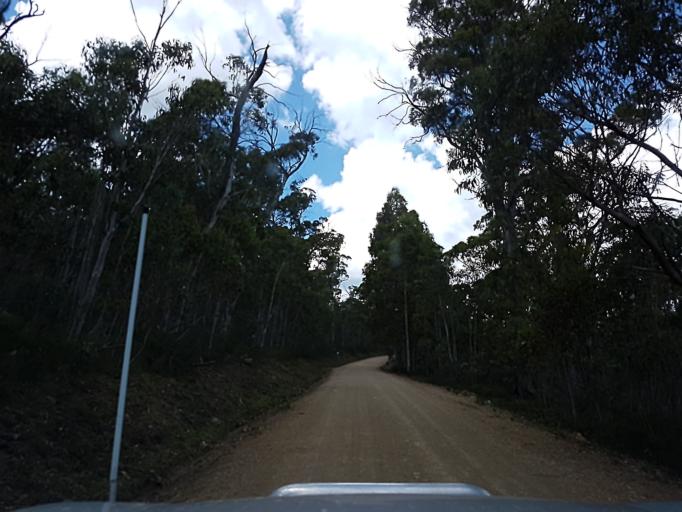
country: AU
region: New South Wales
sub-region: Snowy River
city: Jindabyne
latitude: -36.9108
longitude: 148.1192
